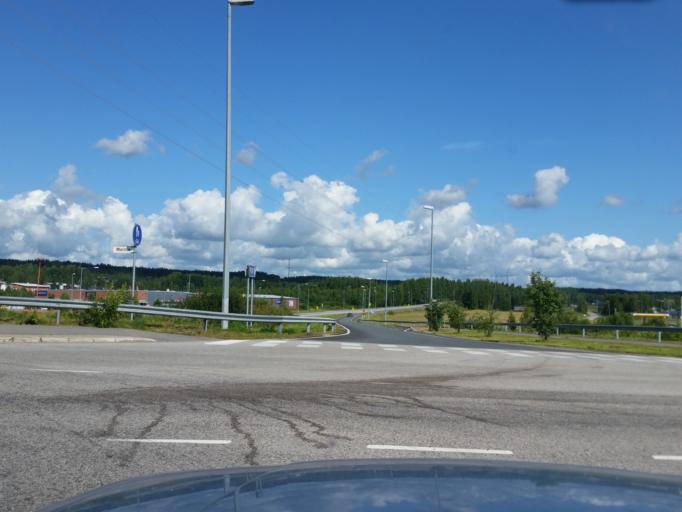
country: FI
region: Uusimaa
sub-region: Helsinki
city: Vihti
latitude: 60.3319
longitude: 24.3340
